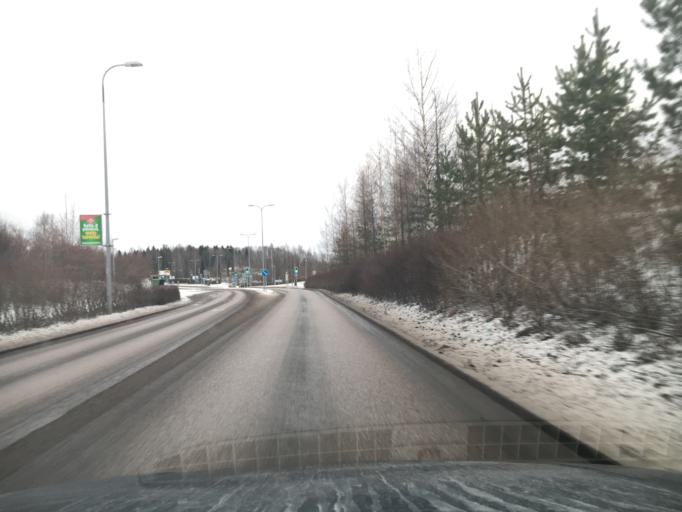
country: FI
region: Uusimaa
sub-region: Helsinki
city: Espoo
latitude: 60.1660
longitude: 24.6603
